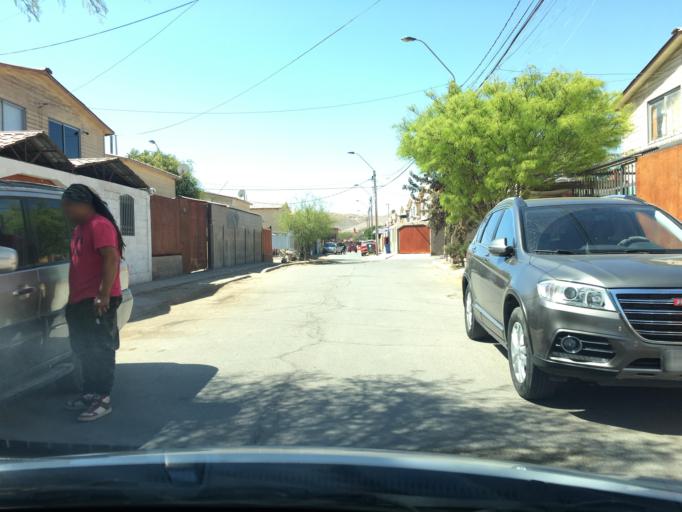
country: CL
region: Atacama
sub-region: Provincia de Copiapo
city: Copiapo
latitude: -27.4082
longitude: -70.2845
